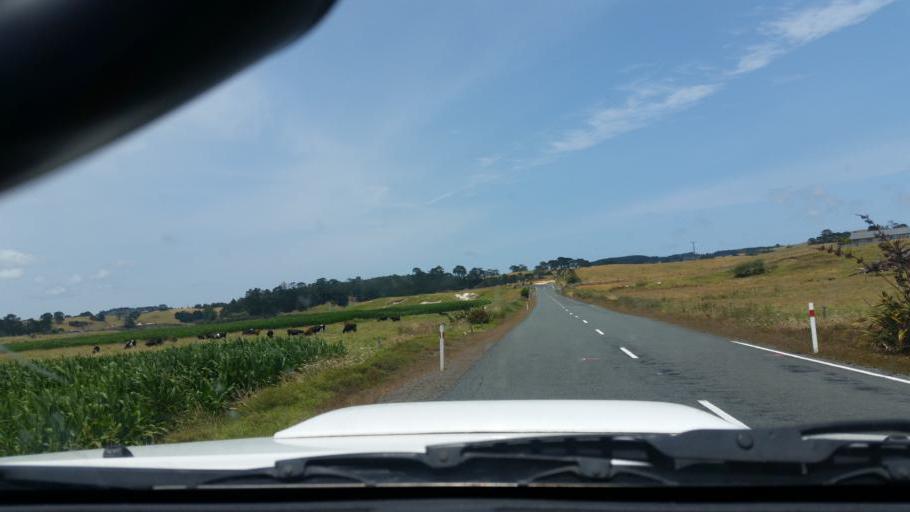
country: NZ
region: Northland
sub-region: Kaipara District
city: Dargaville
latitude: -36.1845
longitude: 174.0326
